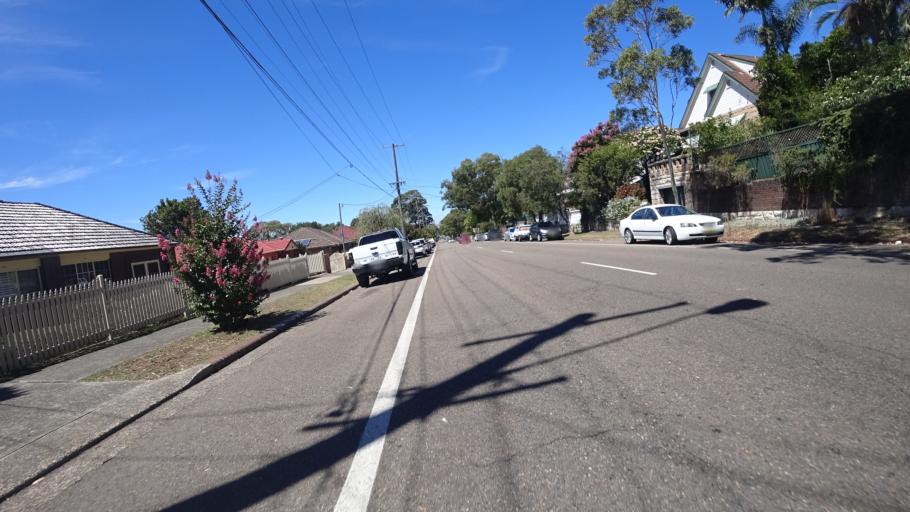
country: AU
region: New South Wales
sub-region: Rockdale
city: Bardwell Valley
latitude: -33.9389
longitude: 151.1374
